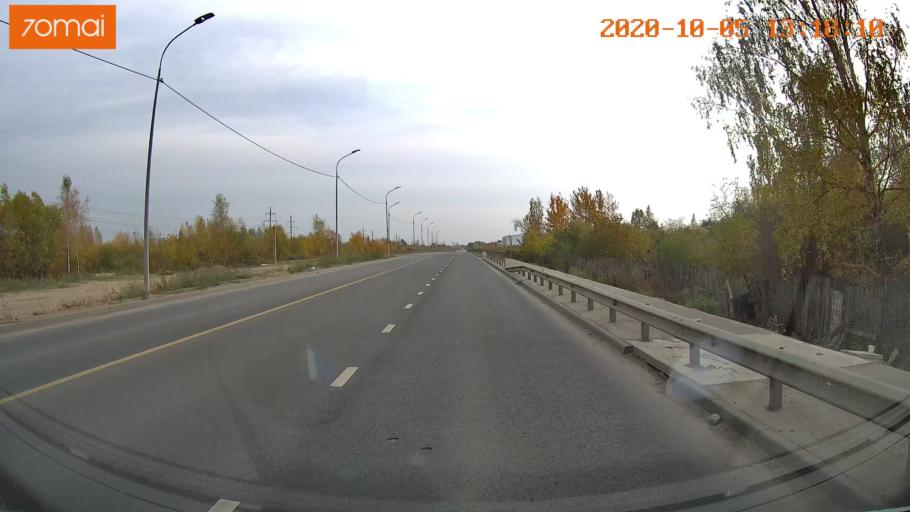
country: RU
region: Ivanovo
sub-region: Gorod Ivanovo
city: Ivanovo
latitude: 56.9797
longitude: 40.9173
